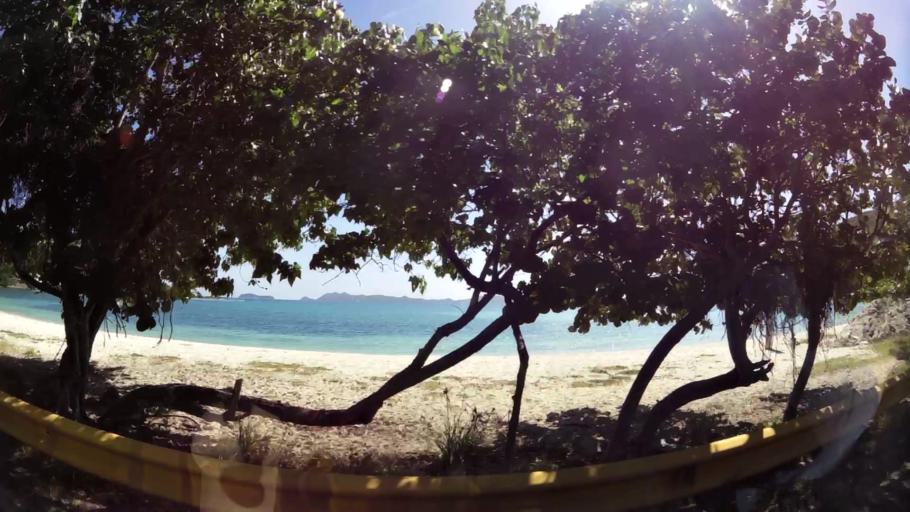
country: VG
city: Tortola
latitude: 18.4168
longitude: -64.5853
